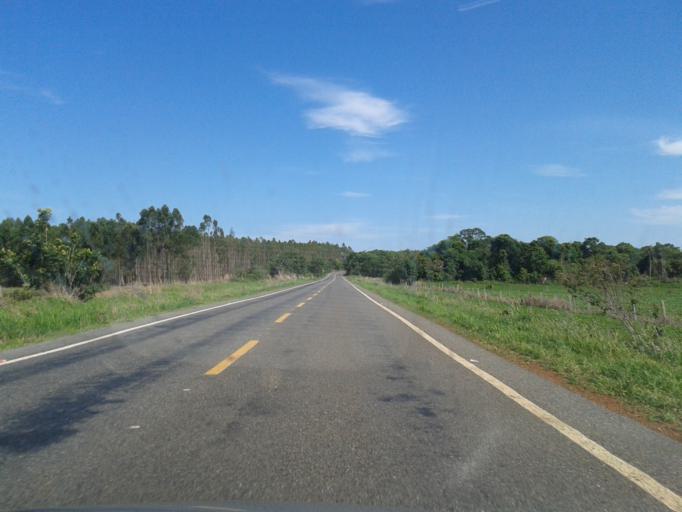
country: BR
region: Goias
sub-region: Piracanjuba
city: Piracanjuba
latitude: -17.3327
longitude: -48.7984
